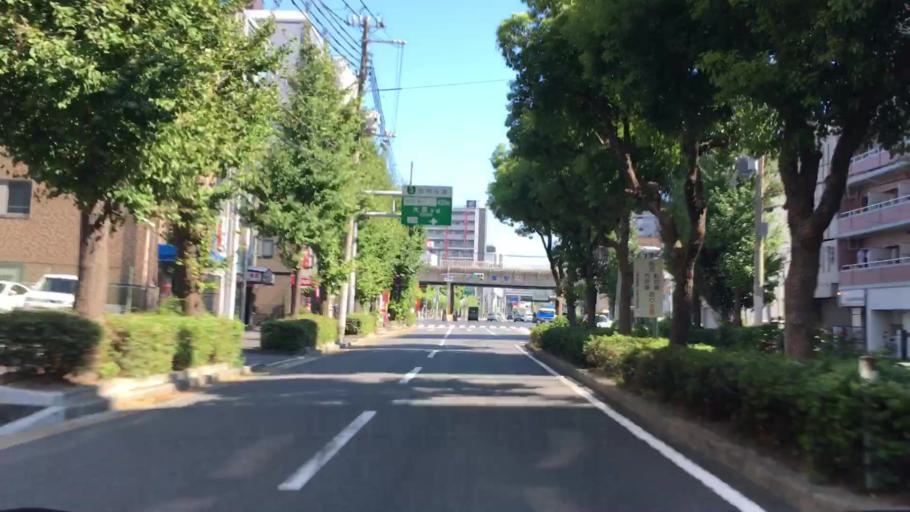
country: JP
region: Hyogo
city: Kobe
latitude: 34.6707
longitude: 135.1666
